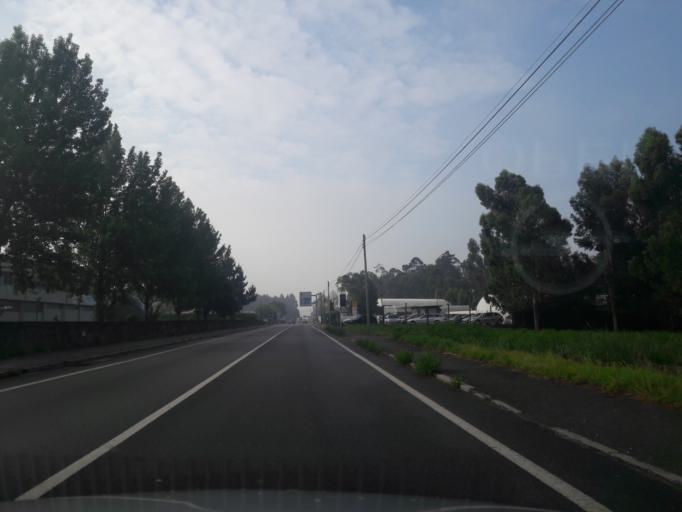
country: PT
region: Porto
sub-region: Vila do Conde
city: Arvore
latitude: 41.3094
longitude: -8.7053
